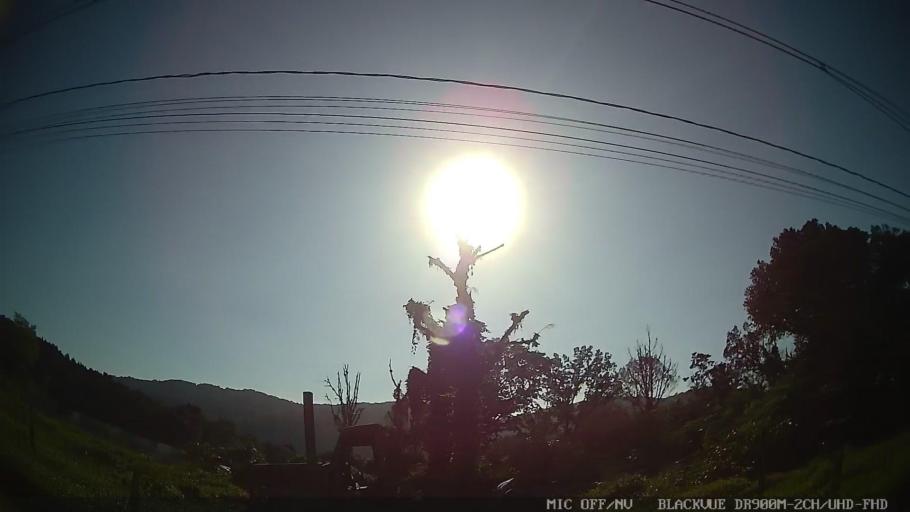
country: BR
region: Sao Paulo
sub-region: Guaruja
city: Guaruja
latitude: -23.9688
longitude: -46.2139
